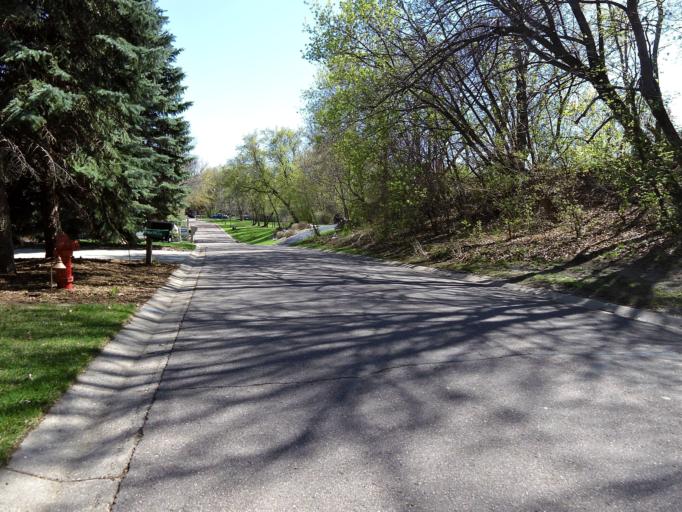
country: US
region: Minnesota
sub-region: Scott County
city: Prior Lake
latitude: 44.7237
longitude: -93.4363
